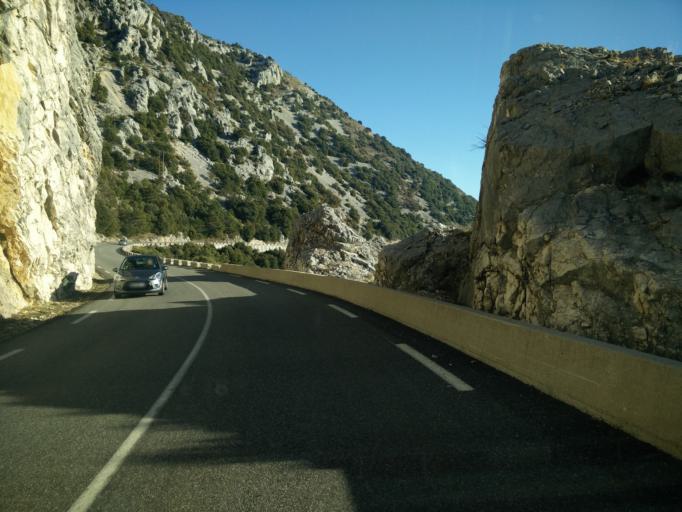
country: FR
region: Provence-Alpes-Cote d'Azur
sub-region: Departement des Alpes-Maritimes
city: Saint-Vallier-de-Thiey
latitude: 43.7288
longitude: 6.8124
